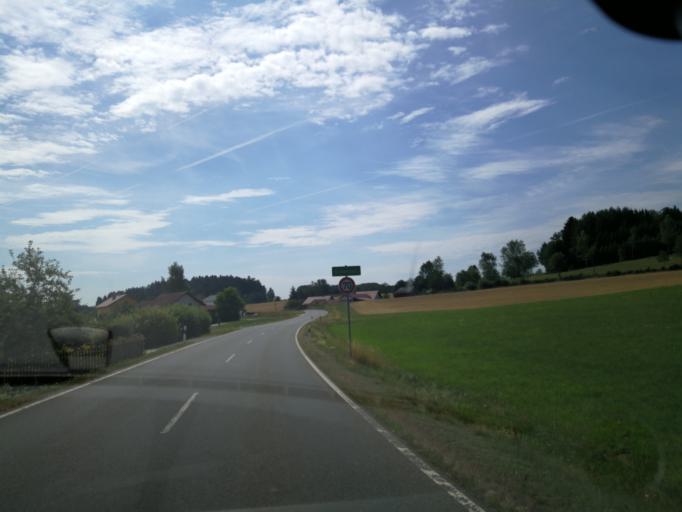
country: DE
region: Bavaria
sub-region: Upper Palatinate
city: Falkenstein
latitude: 49.0848
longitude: 12.5054
